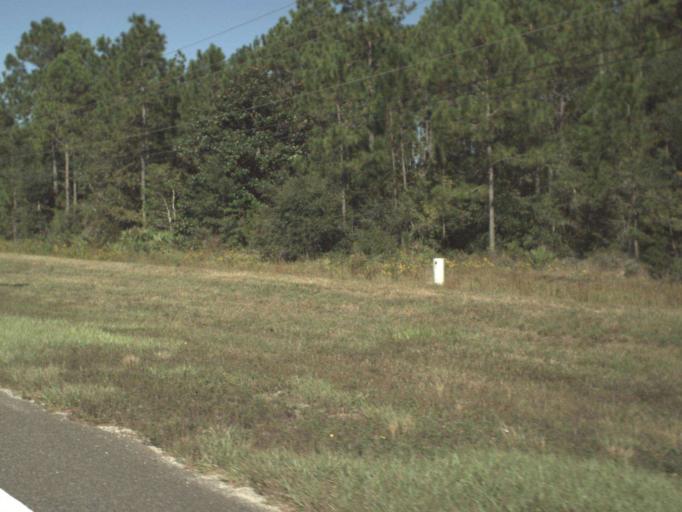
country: US
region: Florida
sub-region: Walton County
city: Seaside
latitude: 30.3569
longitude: -86.1123
